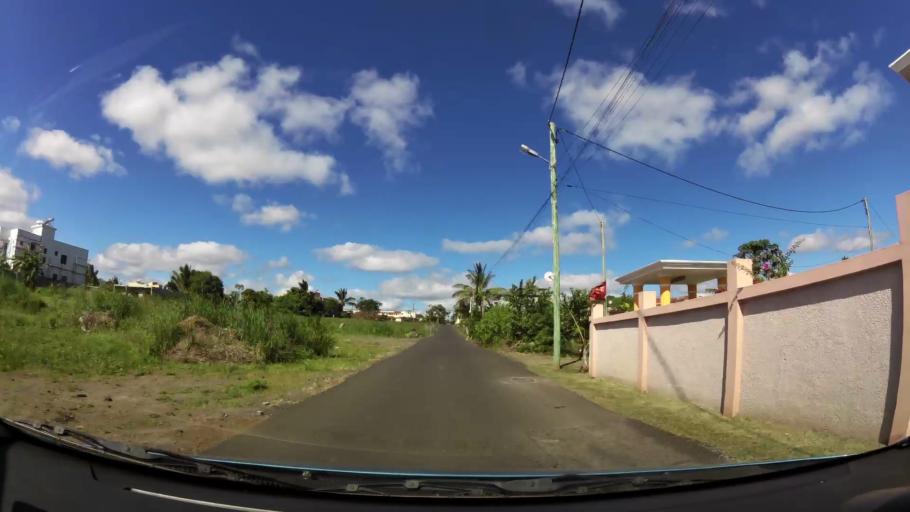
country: MU
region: Plaines Wilhems
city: Vacoas
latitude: -20.2835
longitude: 57.4753
